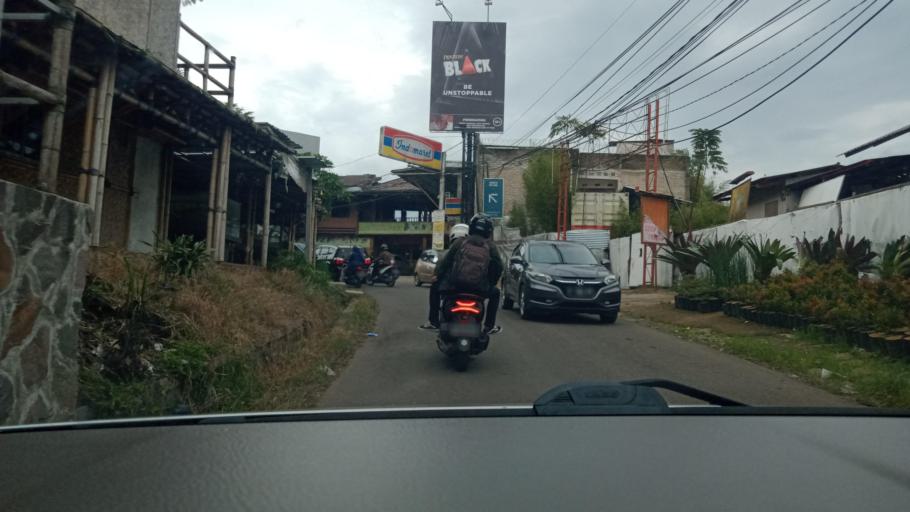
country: ID
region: West Java
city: Lembang
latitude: -6.8216
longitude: 107.5972
